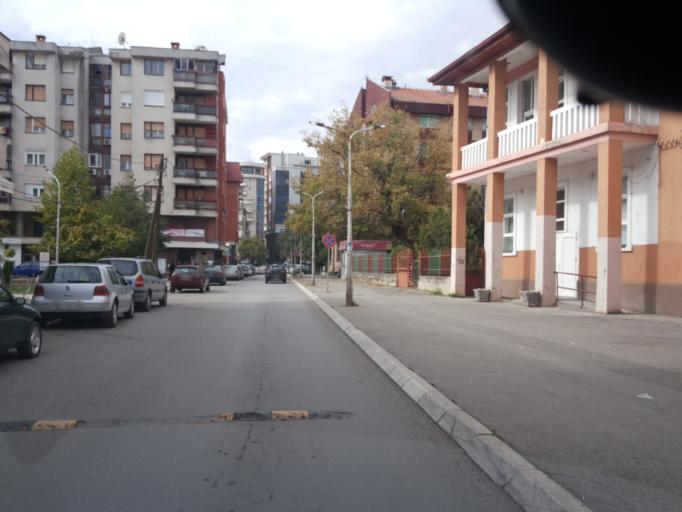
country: XK
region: Gjakova
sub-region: Komuna e Gjakoves
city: Gjakove
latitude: 42.3842
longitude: 20.4327
